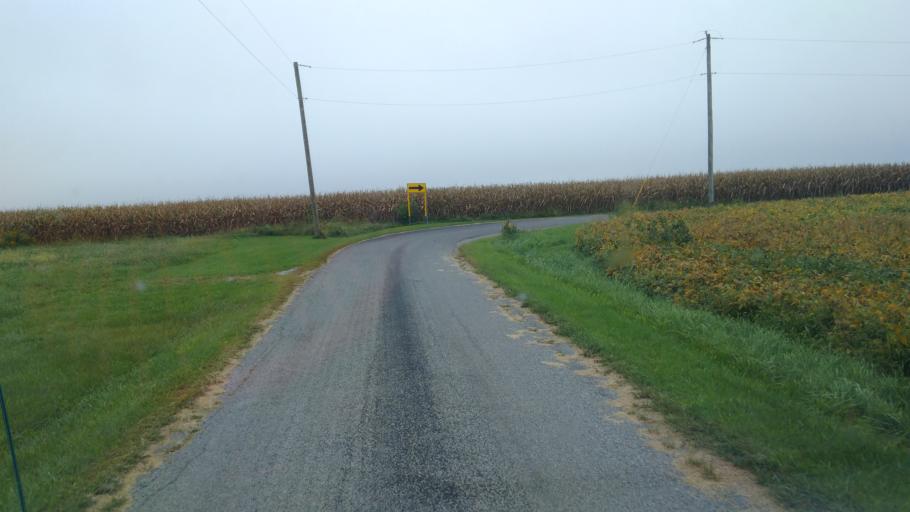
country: US
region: Ohio
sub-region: Union County
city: Richwood
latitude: 40.4946
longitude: -83.3705
